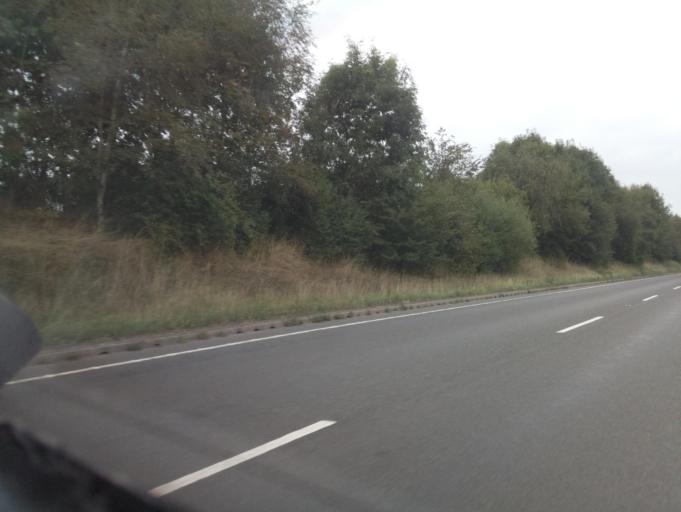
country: GB
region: England
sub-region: Shropshire
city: Stoke upon Tern
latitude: 52.8647
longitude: -2.5554
